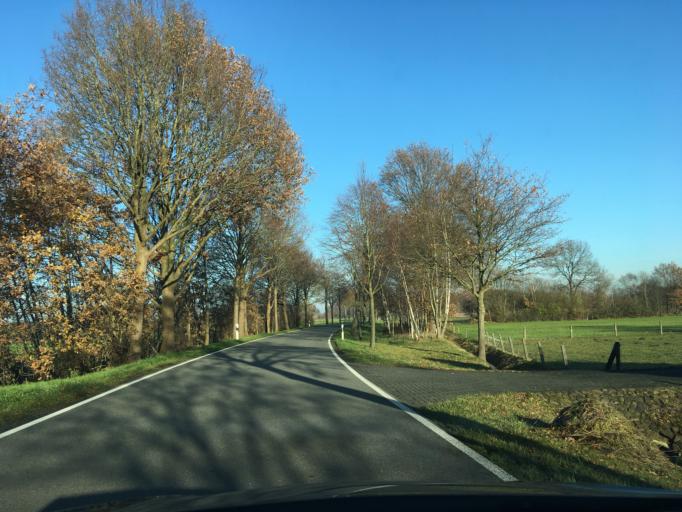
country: DE
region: North Rhine-Westphalia
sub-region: Regierungsbezirk Munster
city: Vreden
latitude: 52.1136
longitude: 6.8830
